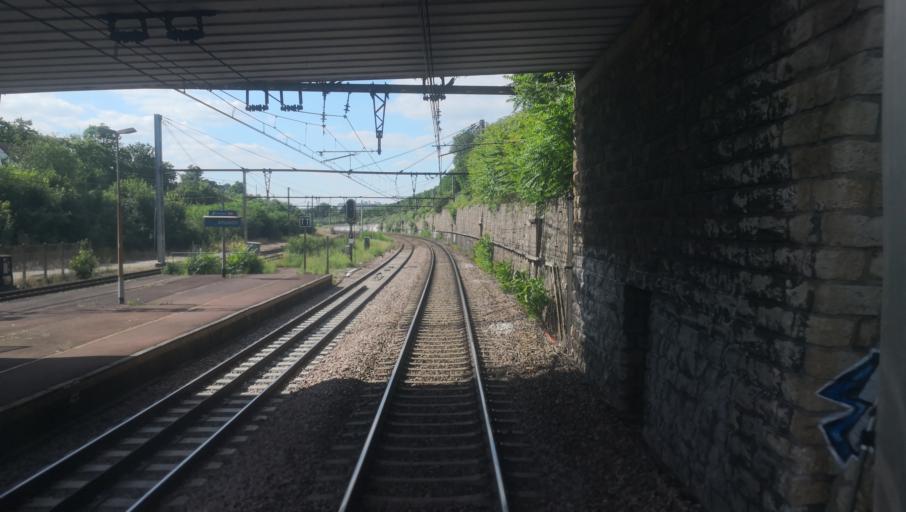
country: FR
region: Ile-de-France
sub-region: Departement de l'Essonne
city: Epinay-sous-Senart
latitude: 48.7005
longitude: 2.5057
